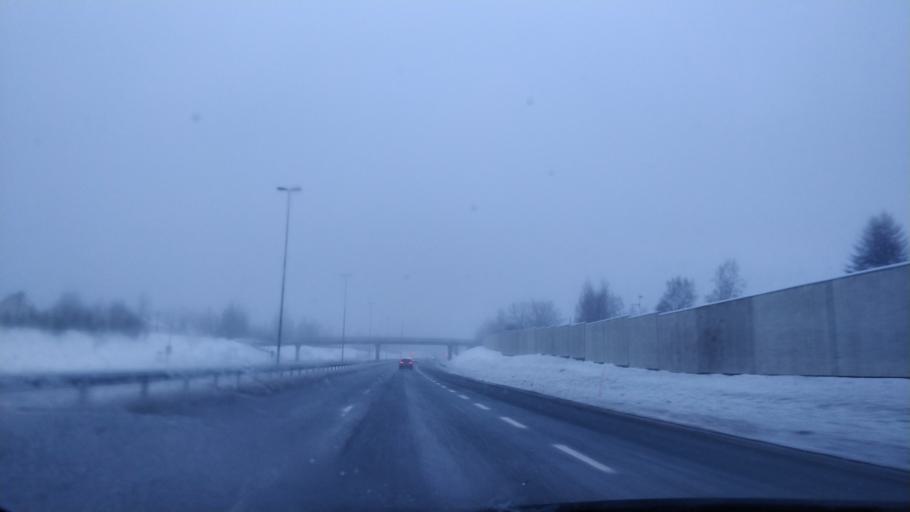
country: FI
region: Lapland
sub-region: Kemi-Tornio
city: Kemi
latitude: 65.7451
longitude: 24.5817
